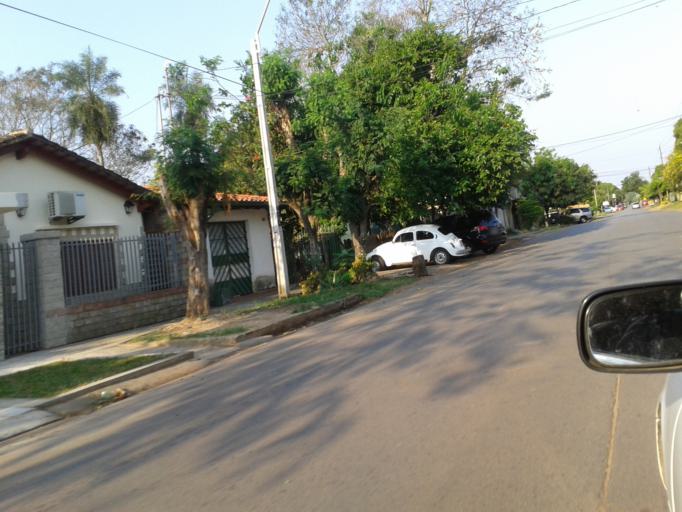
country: PY
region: Guaira
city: Villarrica
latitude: -25.7706
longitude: -56.4440
